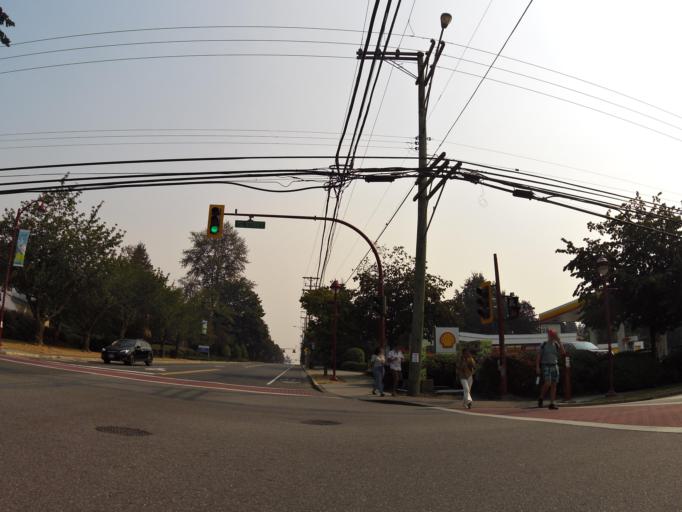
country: CA
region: British Columbia
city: Delta
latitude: 49.1560
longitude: -122.9125
